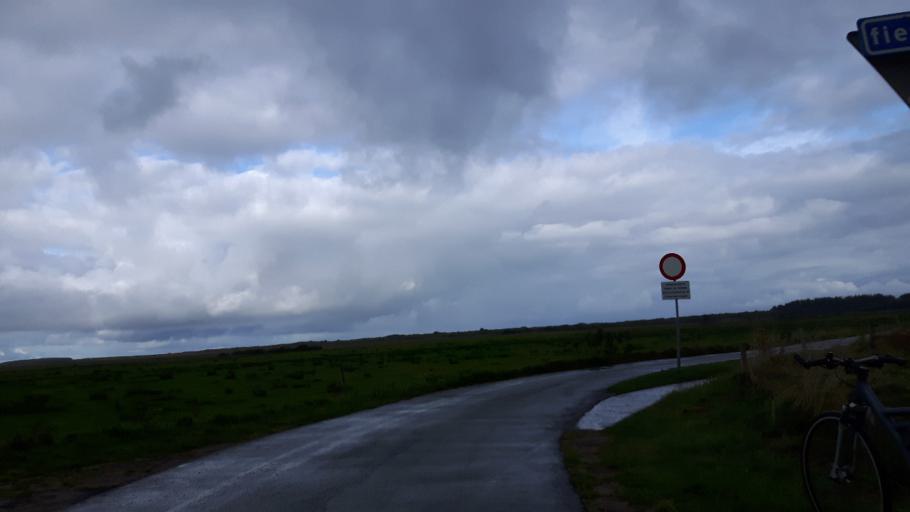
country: NL
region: Friesland
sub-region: Gemeente Ameland
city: Nes
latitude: 53.4461
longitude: 5.7578
